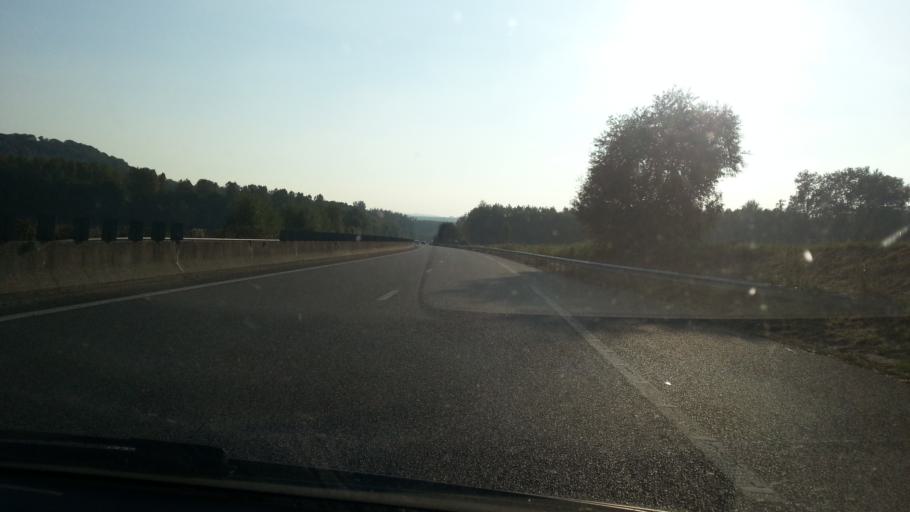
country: FR
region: Picardie
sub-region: Departement de l'Oise
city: Coudun
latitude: 49.4714
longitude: 2.8312
